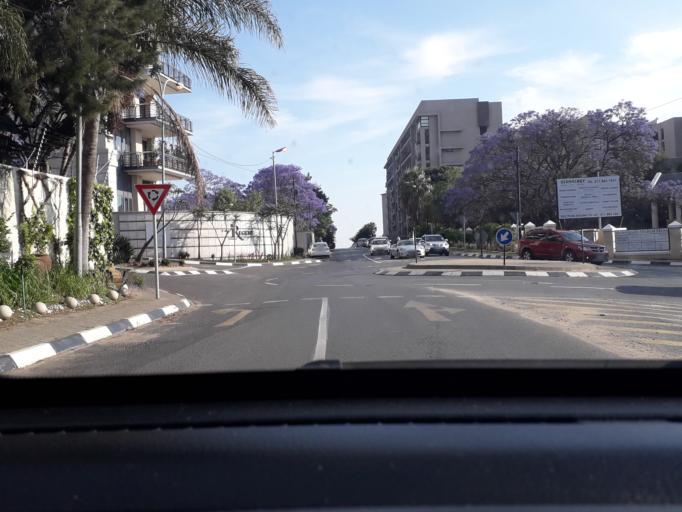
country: ZA
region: Gauteng
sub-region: City of Johannesburg Metropolitan Municipality
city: Johannesburg
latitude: -26.0935
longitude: 28.0543
